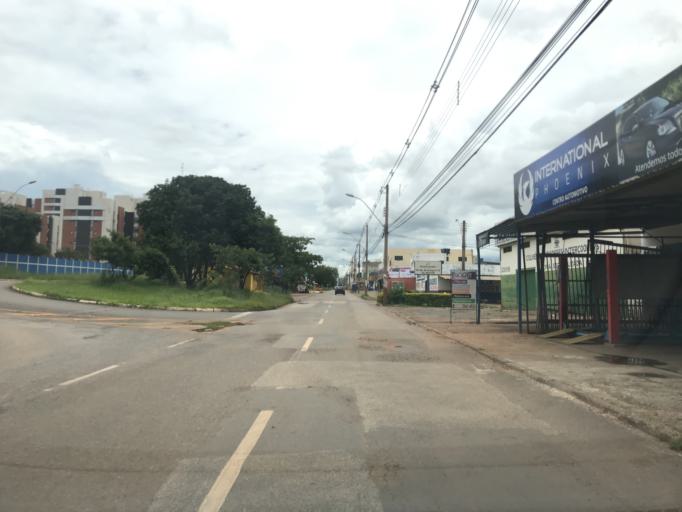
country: BR
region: Federal District
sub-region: Brasilia
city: Brasilia
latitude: -15.8212
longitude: -47.9561
